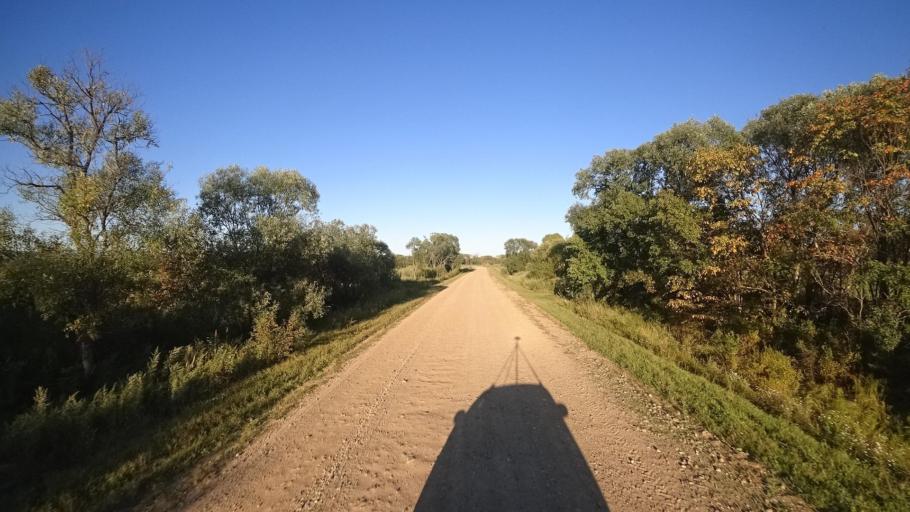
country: RU
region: Primorskiy
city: Kirovskiy
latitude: 44.8315
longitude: 133.5824
